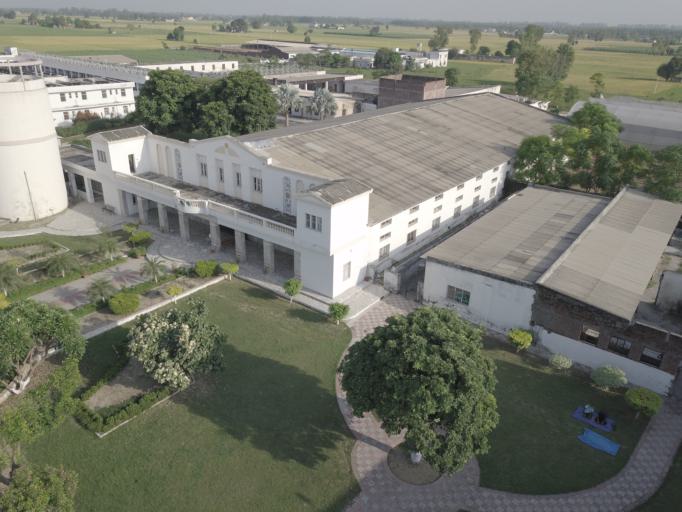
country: IN
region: Punjab
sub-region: Shahid Bhagat Singh Nagar
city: Rahon
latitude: 31.0196
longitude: 76.0909
